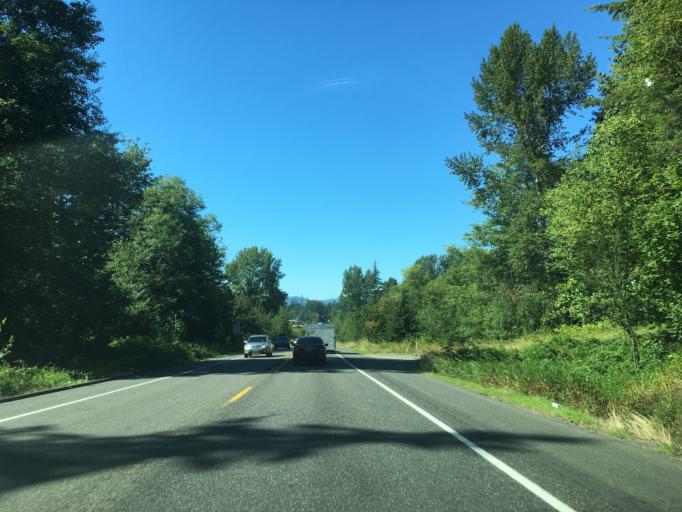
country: US
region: Washington
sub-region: Snohomish County
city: Arlington
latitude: 48.1752
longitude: -122.1263
